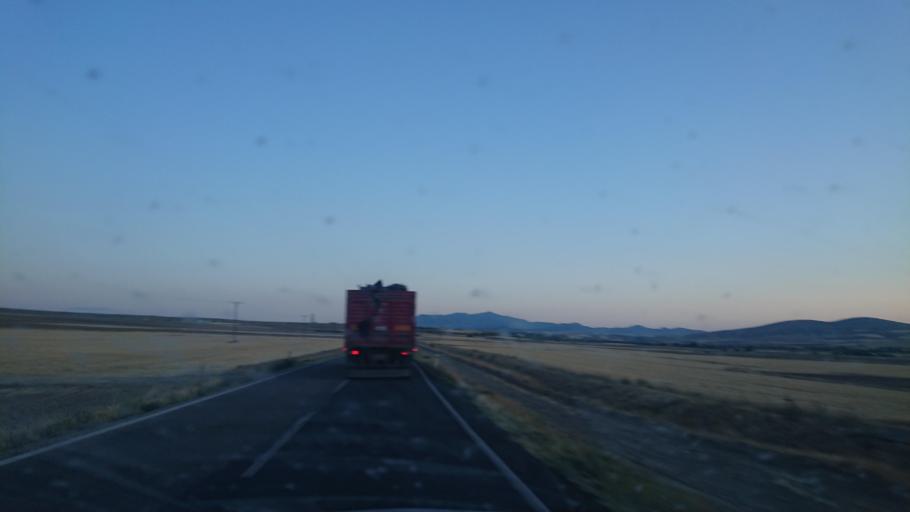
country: TR
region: Aksaray
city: Balci
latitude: 38.8157
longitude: 34.1342
